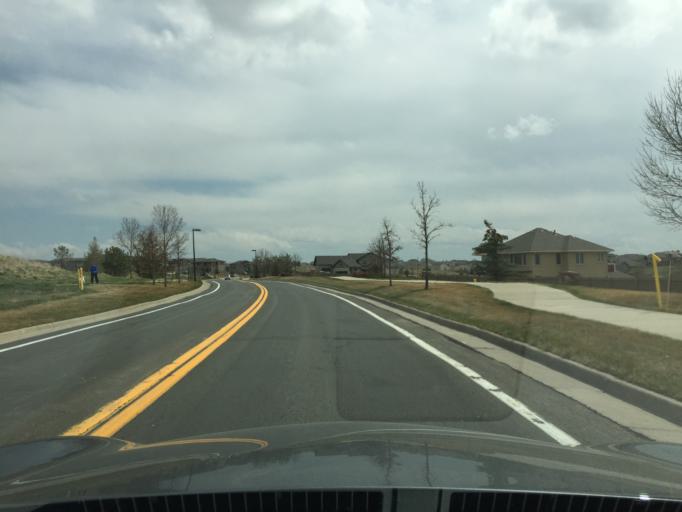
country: US
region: Colorado
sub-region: Boulder County
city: Erie
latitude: 40.0148
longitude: -105.0362
